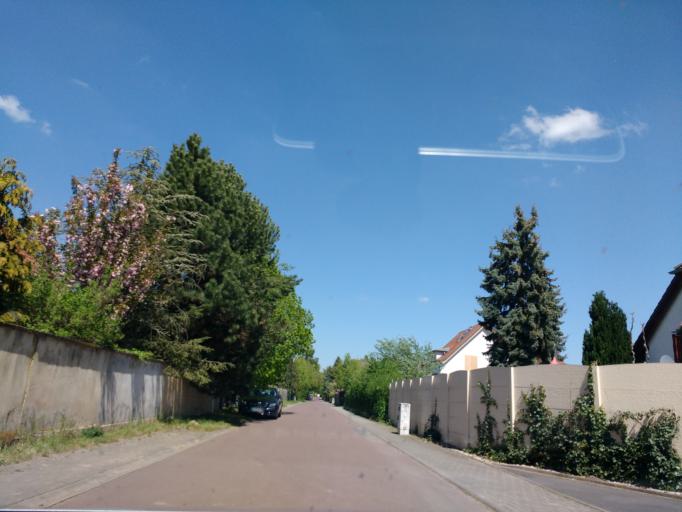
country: DE
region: Saxony-Anhalt
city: Peissen
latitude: 51.4891
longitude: 12.0389
